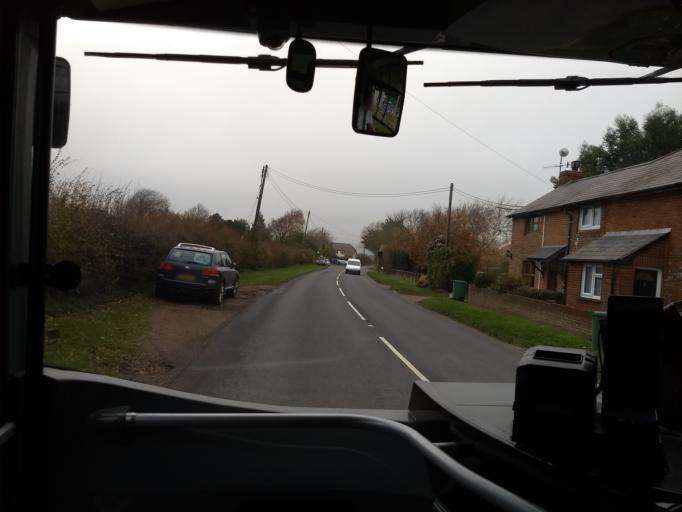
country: GB
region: England
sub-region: Isle of Wight
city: Newchurch
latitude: 50.6574
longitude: -1.2257
